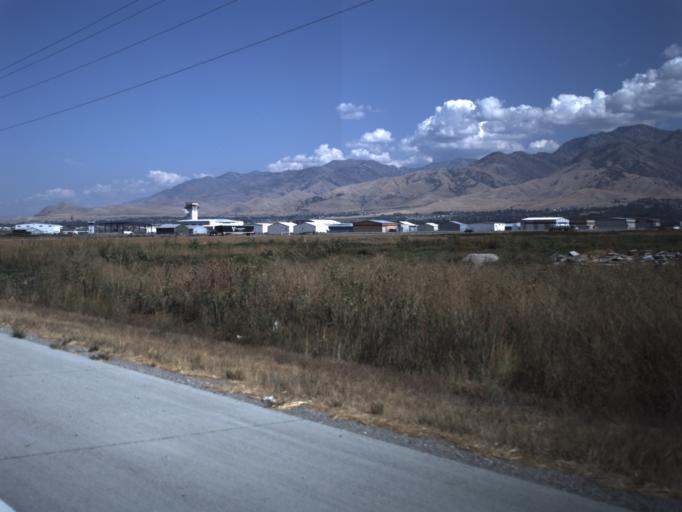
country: US
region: Utah
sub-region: Cache County
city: Hyde Park
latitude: 41.7751
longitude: -111.8577
